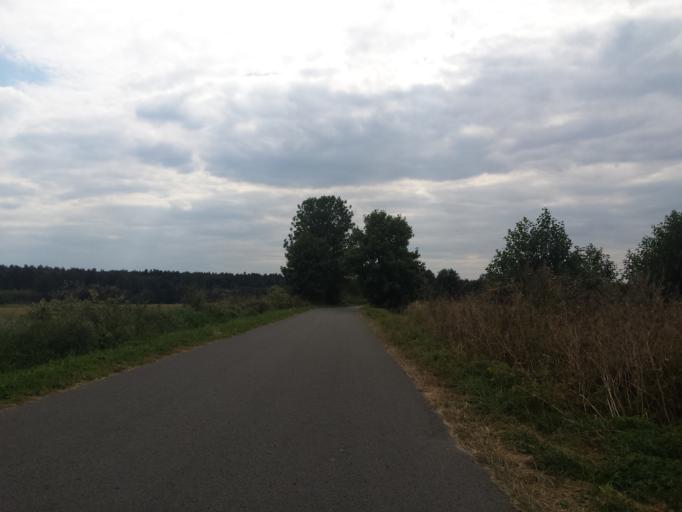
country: PL
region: Swietokrzyskie
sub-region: Powiat staszowski
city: Bogoria
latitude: 50.6595
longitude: 21.2303
